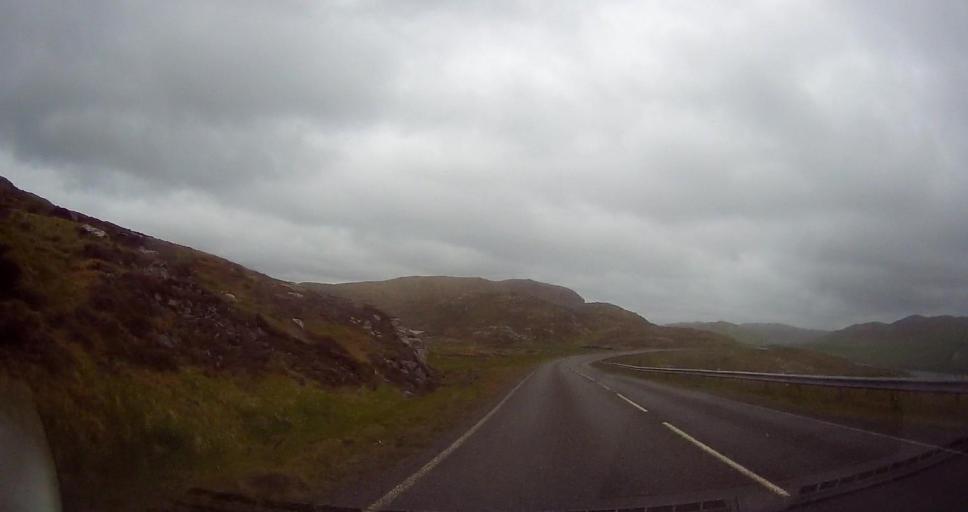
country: GB
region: Scotland
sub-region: Shetland Islands
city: Lerwick
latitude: 60.4182
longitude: -1.3939
